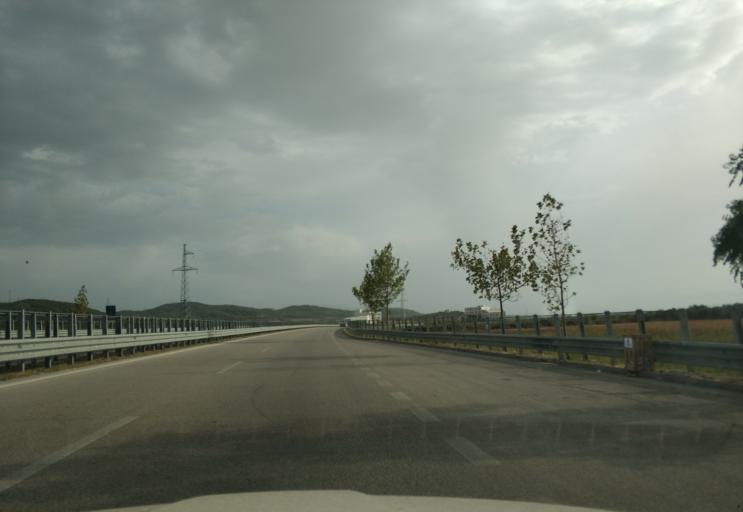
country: AL
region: Vlore
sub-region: Rrethi i Vlores
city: Novosele
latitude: 40.6052
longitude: 19.4769
